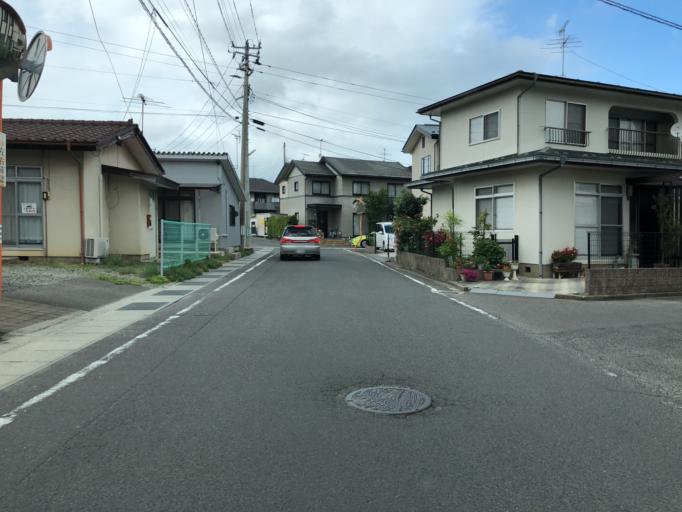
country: JP
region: Fukushima
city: Fukushima-shi
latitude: 37.7796
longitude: 140.4577
